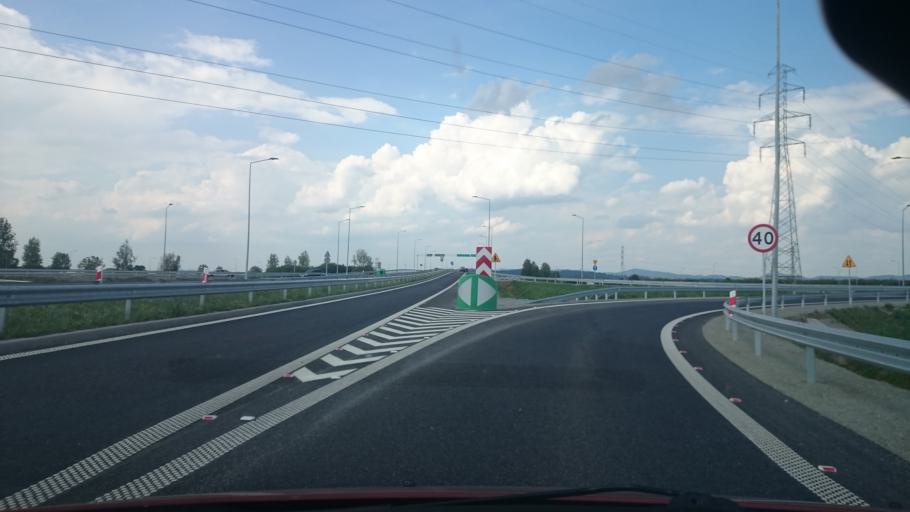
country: PL
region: Lower Silesian Voivodeship
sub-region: Powiat klodzki
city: Klodzko
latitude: 50.4361
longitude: 16.6278
